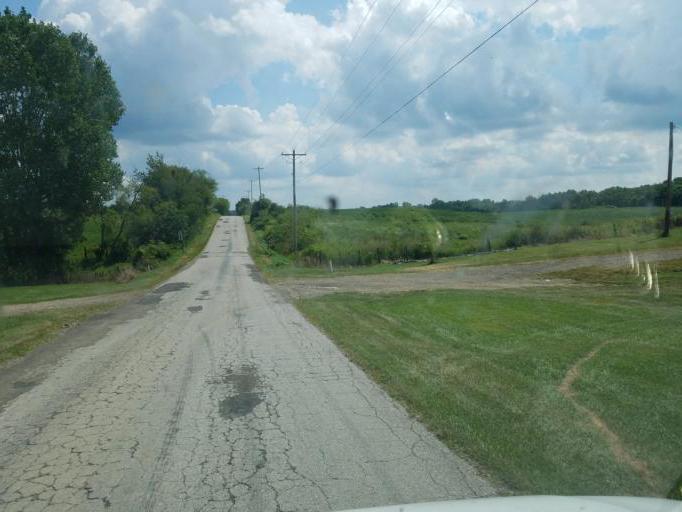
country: US
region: Ohio
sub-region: Knox County
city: Centerburg
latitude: 40.4073
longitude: -82.6754
